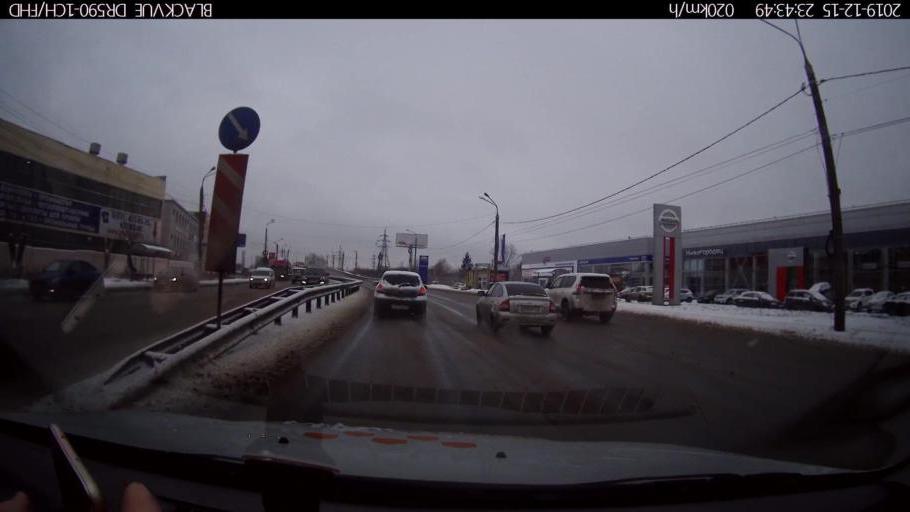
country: RU
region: Nizjnij Novgorod
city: Nizhniy Novgorod
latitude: 56.3103
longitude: 43.9015
